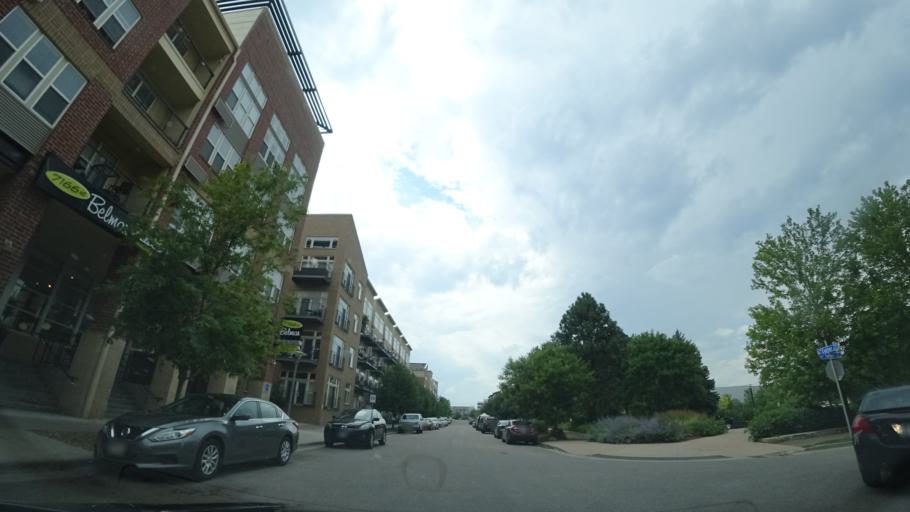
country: US
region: Colorado
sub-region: Jefferson County
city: Lakewood
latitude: 39.7062
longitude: -105.0759
